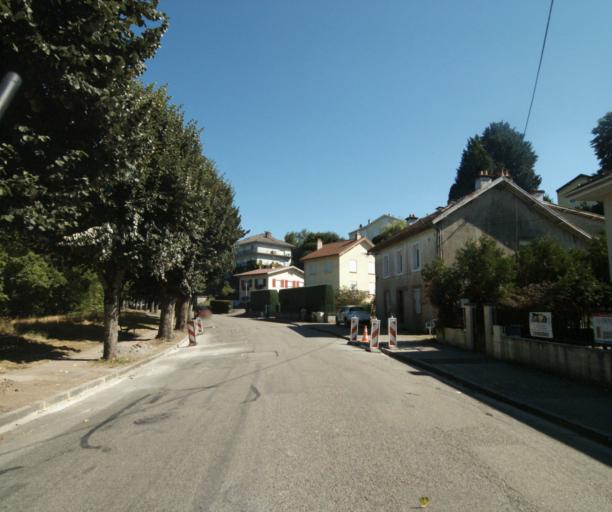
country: FR
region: Lorraine
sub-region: Departement des Vosges
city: Chantraine
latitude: 48.1600
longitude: 6.4564
